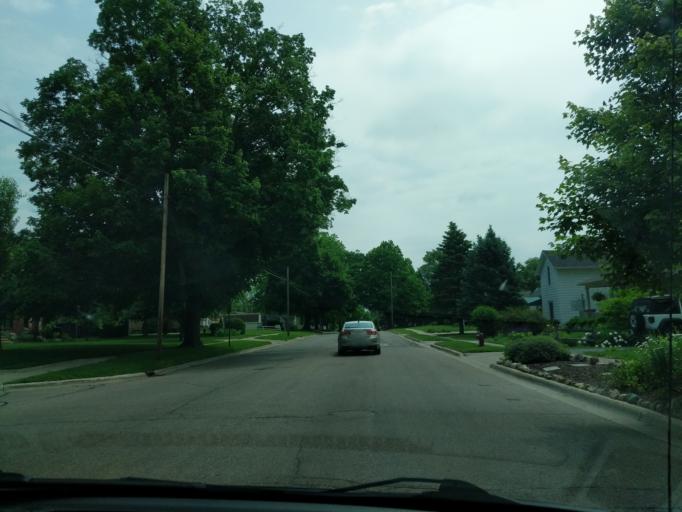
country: US
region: Michigan
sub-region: Ingham County
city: Williamston
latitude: 42.6937
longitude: -84.2825
